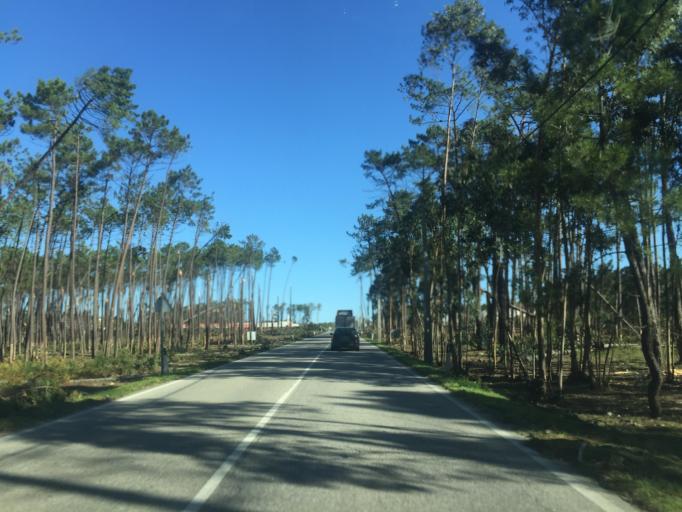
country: PT
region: Leiria
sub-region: Leiria
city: Monte Redondo
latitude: 39.9323
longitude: -8.8014
